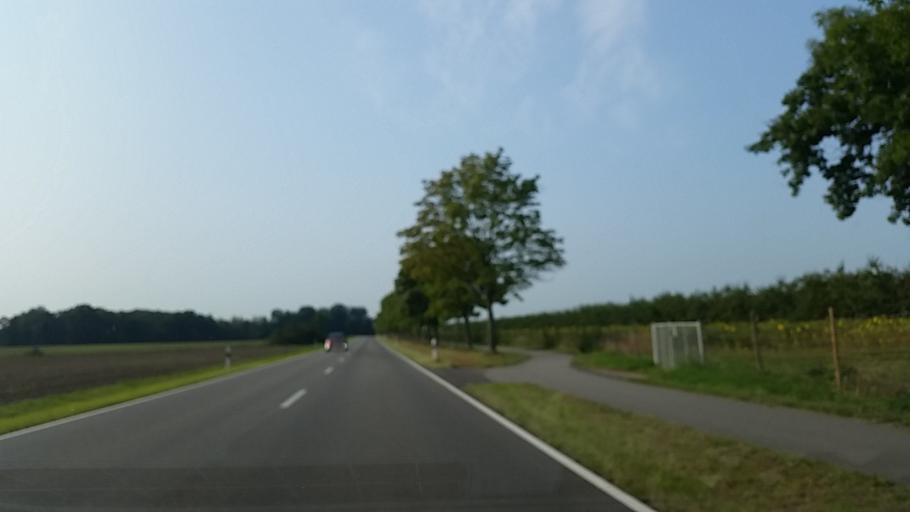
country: DE
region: Mecklenburg-Vorpommern
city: Lubtheen
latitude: 53.3884
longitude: 11.0884
